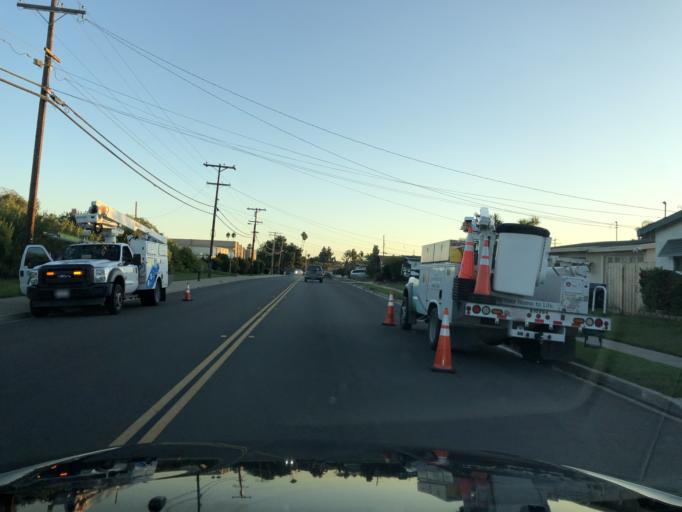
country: US
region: California
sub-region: San Diego County
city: La Jolla
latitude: 32.8293
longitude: -117.1758
